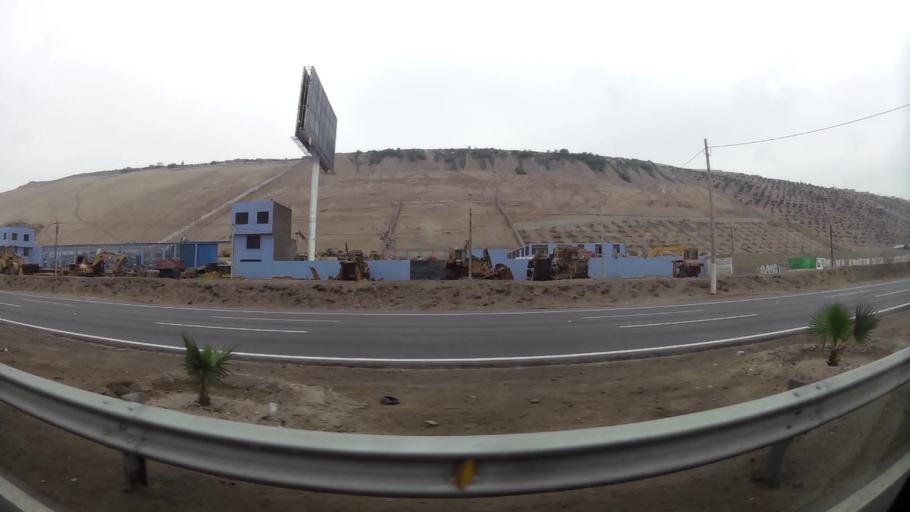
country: PE
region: Lima
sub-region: Lima
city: Surco
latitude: -12.2445
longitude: -76.9401
